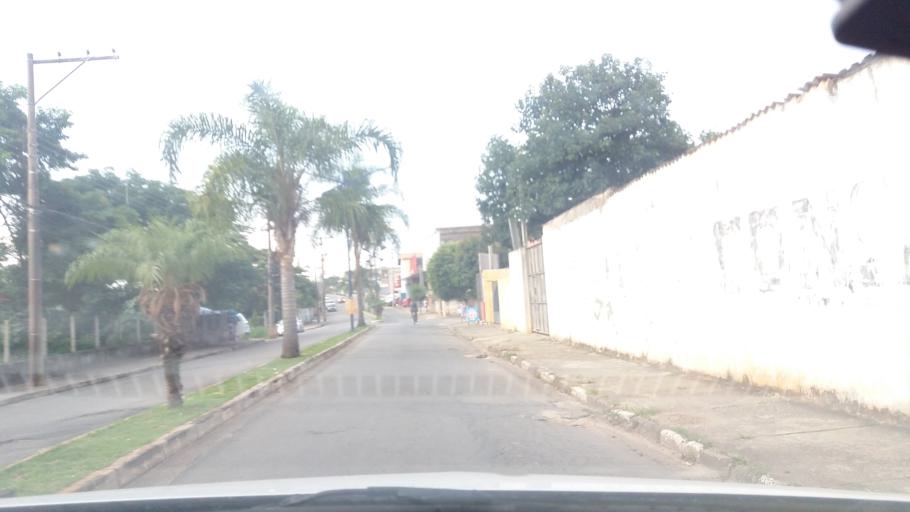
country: BR
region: Sao Paulo
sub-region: Bom Jesus Dos Perdoes
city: Bom Jesus dos Perdoes
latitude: -23.1428
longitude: -46.4682
